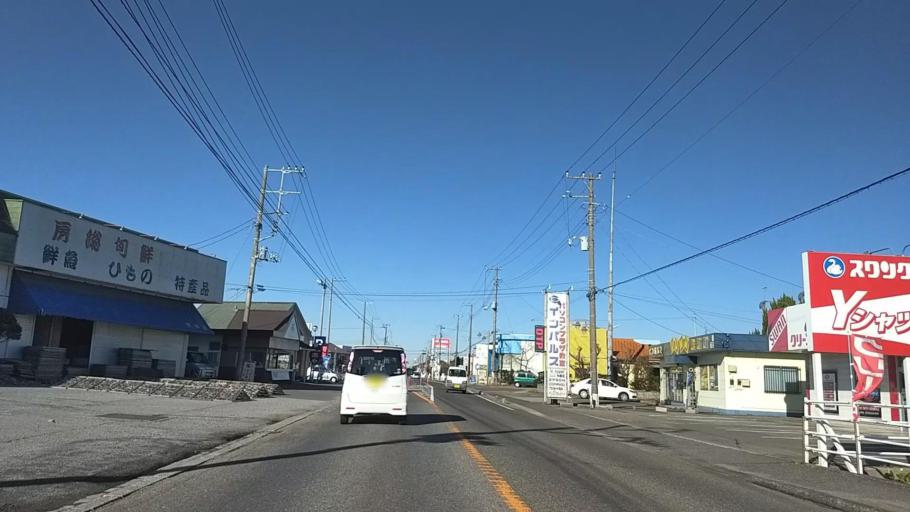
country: JP
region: Chiba
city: Ohara
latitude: 35.2772
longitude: 140.3939
